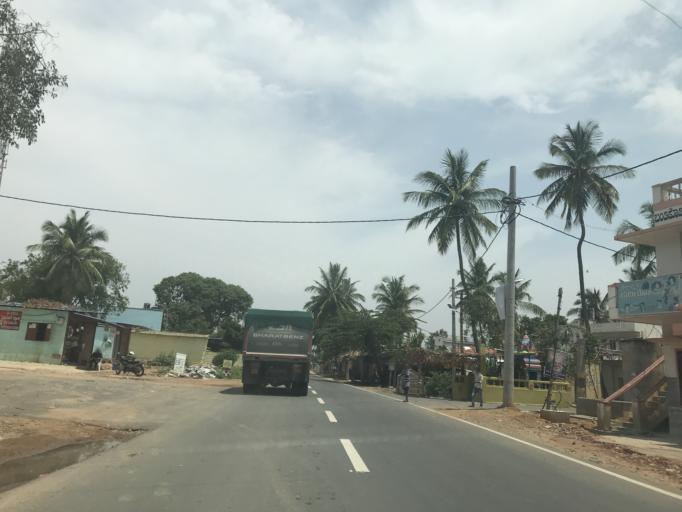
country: IN
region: Karnataka
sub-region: Bangalore Rural
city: Devanhalli
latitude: 13.1725
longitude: 77.6909
